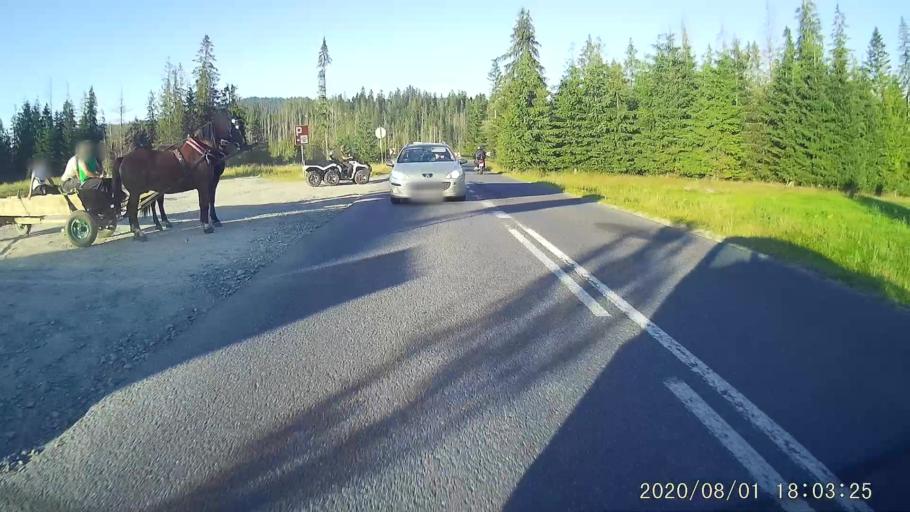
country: PL
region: Lesser Poland Voivodeship
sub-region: Powiat tatrzanski
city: Bukowina Tatrzanska
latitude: 49.2928
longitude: 20.0607
